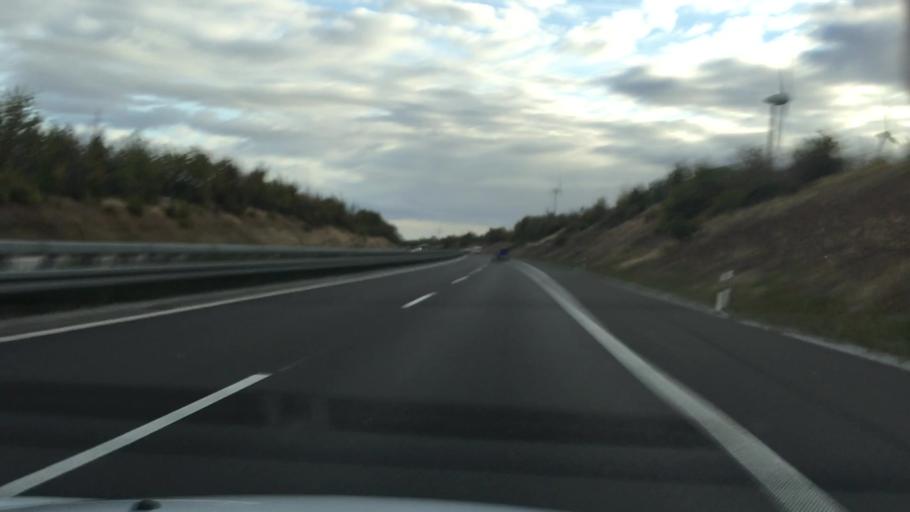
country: DE
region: Saxony-Anhalt
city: Ilberstedt
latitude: 51.7787
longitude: 11.6717
